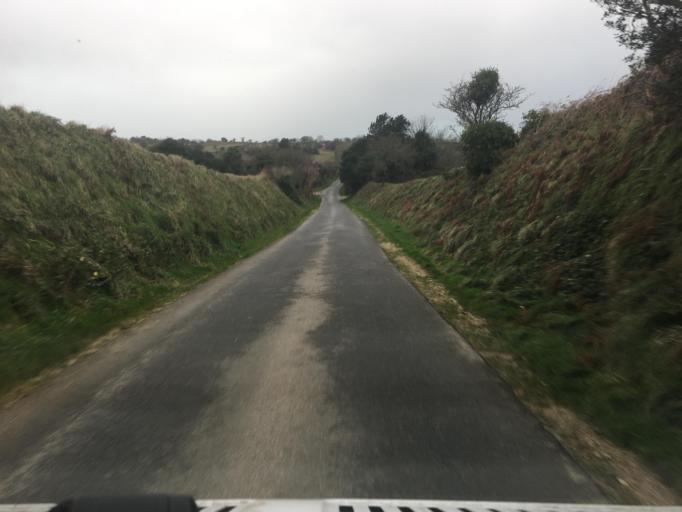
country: FR
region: Lower Normandy
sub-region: Departement de la Manche
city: Beaumont-Hague
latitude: 49.6838
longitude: -1.8632
